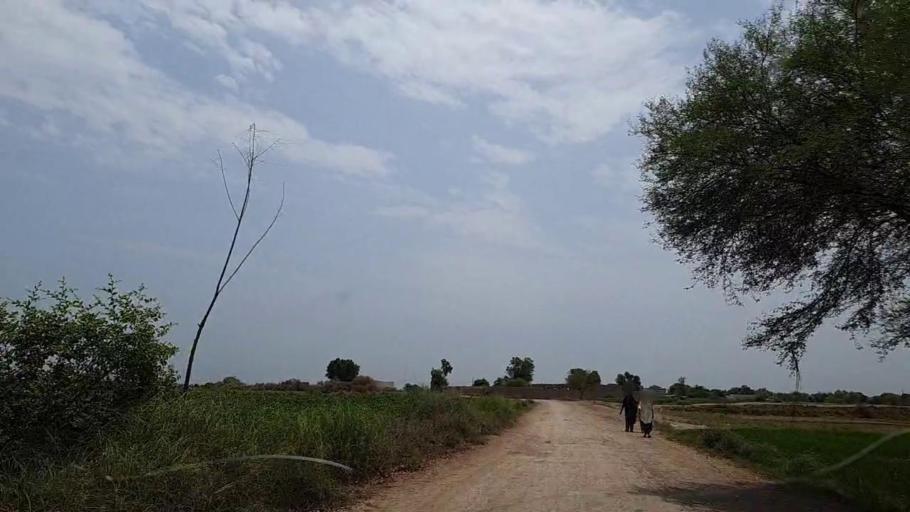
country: PK
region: Sindh
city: Tharu Shah
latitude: 26.9093
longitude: 68.0785
